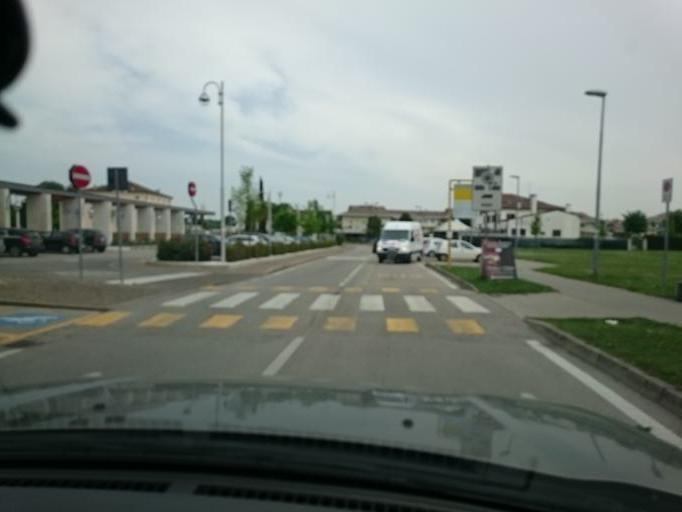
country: IT
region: Veneto
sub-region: Provincia di Padova
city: Noventa
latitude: 45.4124
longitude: 11.9480
